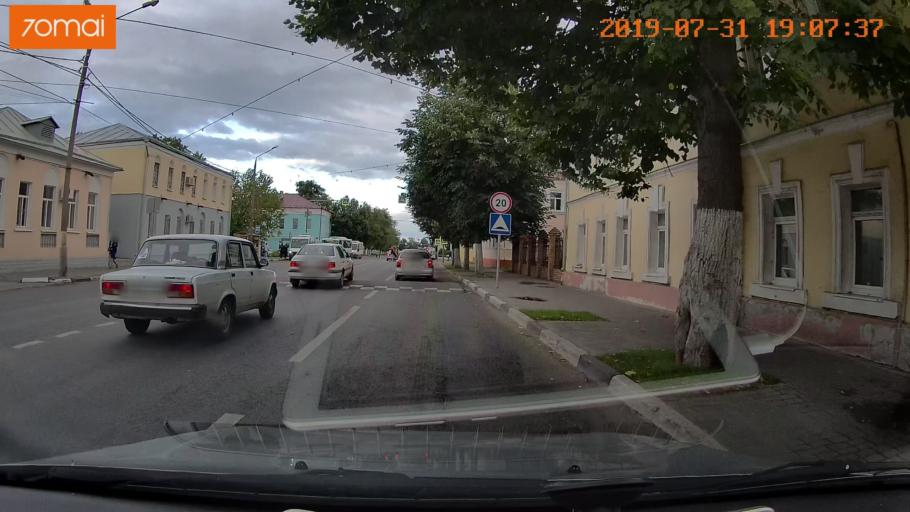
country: RU
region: Moskovskaya
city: Kolomna
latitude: 55.0979
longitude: 38.7613
